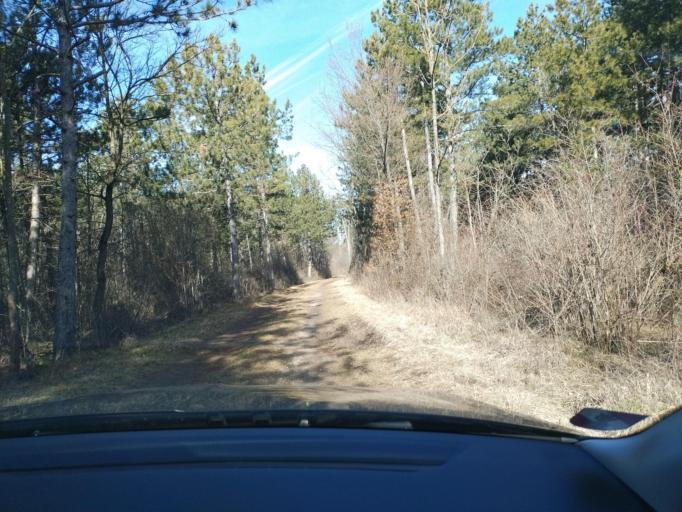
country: AT
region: Lower Austria
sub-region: Politischer Bezirk Neunkirchen
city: Breitenau
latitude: 47.7492
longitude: 16.1612
